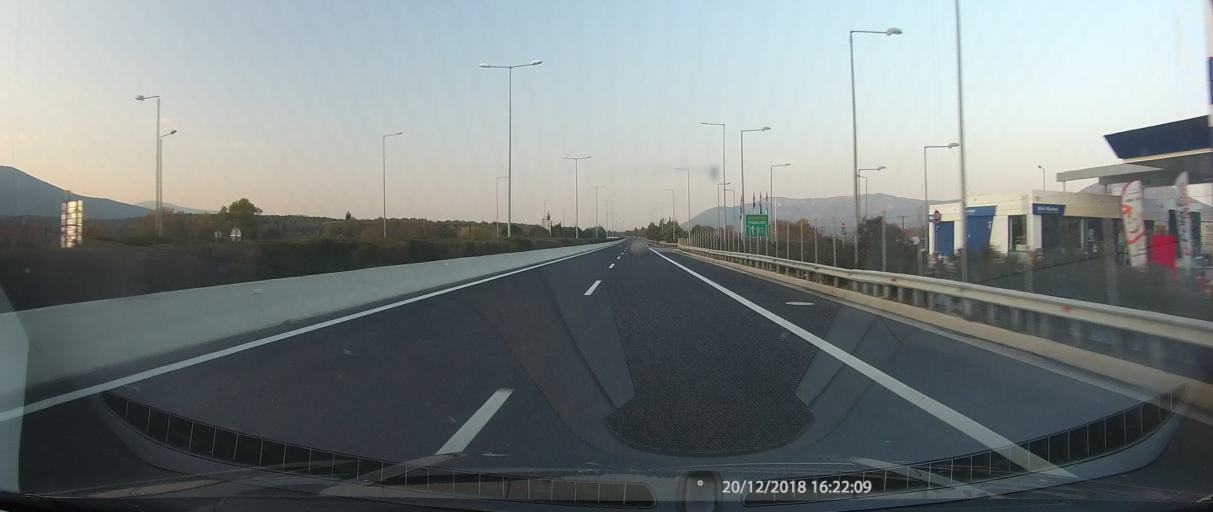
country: GR
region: Thessaly
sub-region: Nomos Magnisias
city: Sourpi
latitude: 39.0637
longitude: 22.8884
